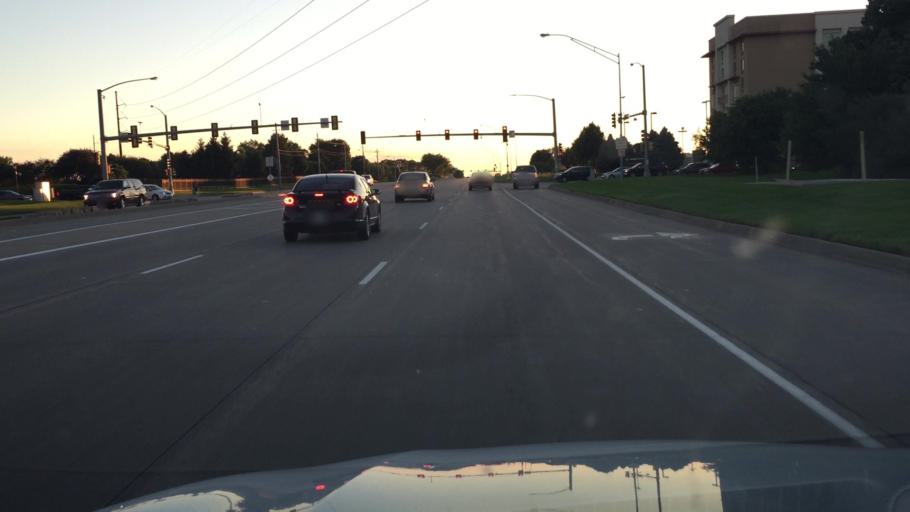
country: US
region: Iowa
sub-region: Polk County
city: Clive
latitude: 41.5592
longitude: -93.7803
